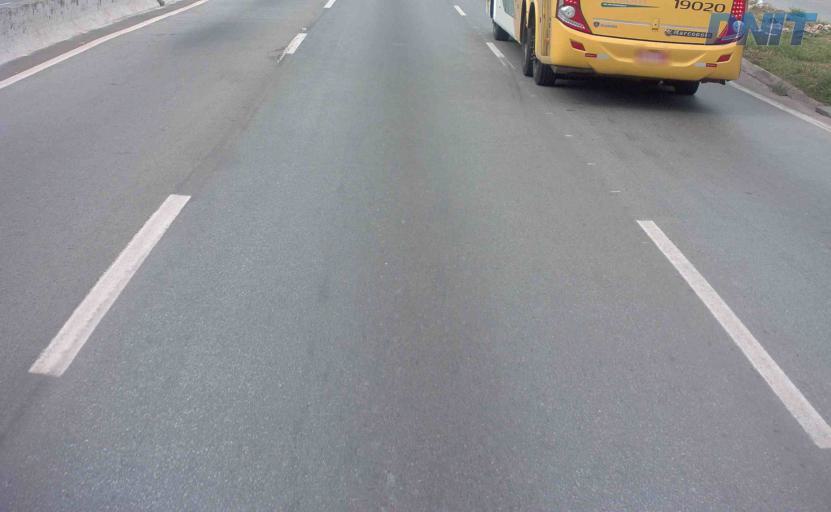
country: BR
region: Minas Gerais
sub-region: Belo Horizonte
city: Belo Horizonte
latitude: -19.8588
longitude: -43.9103
